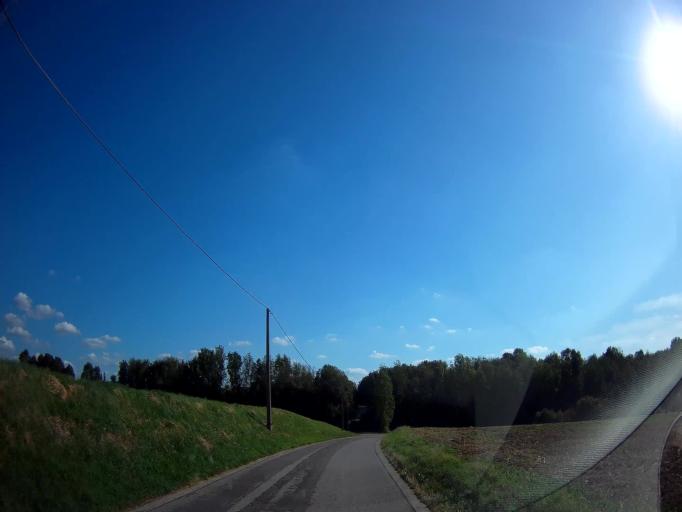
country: BE
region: Wallonia
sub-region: Province de Namur
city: Houyet
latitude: 50.2430
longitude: 4.9867
